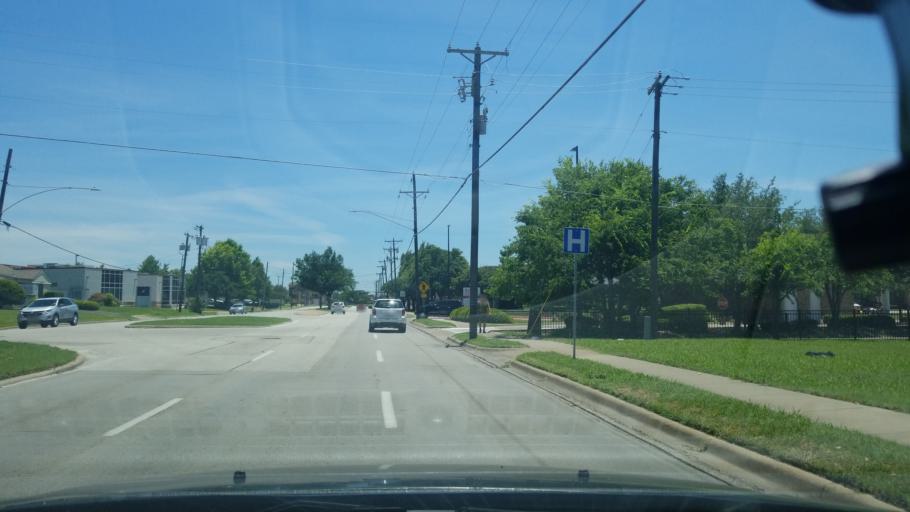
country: US
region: Texas
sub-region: Dallas County
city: Mesquite
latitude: 32.7800
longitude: -96.6004
